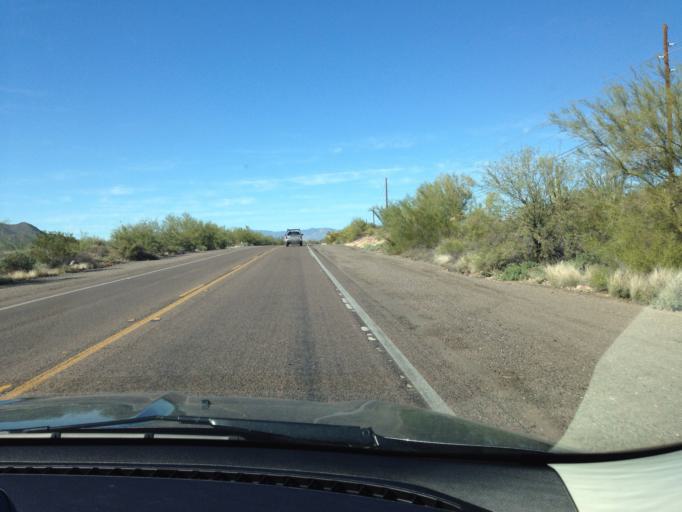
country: US
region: Arizona
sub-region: Maricopa County
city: New River
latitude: 33.8754
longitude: -112.0683
